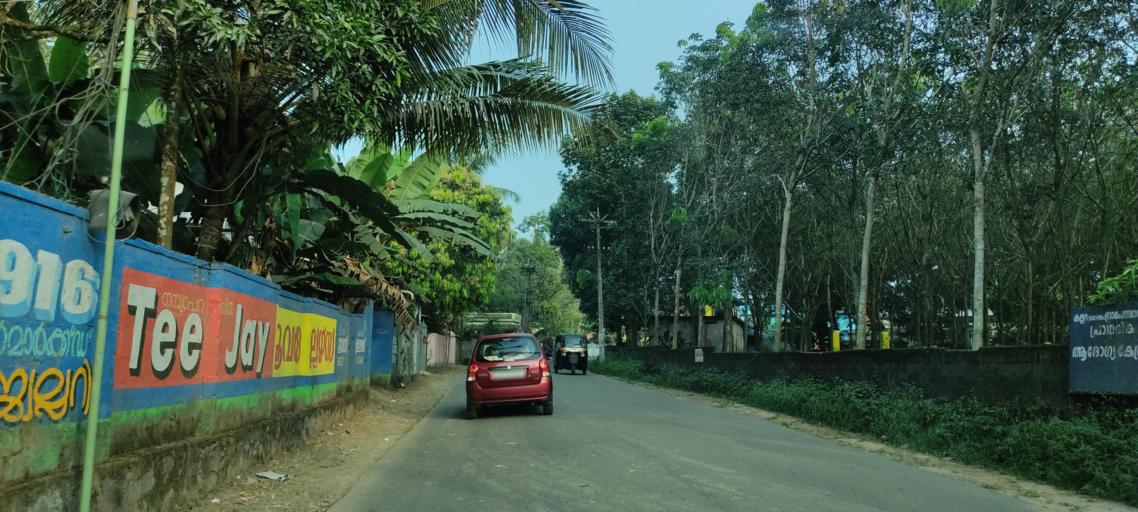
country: IN
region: Kerala
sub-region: Kottayam
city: Vaikam
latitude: 9.7091
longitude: 76.4760
